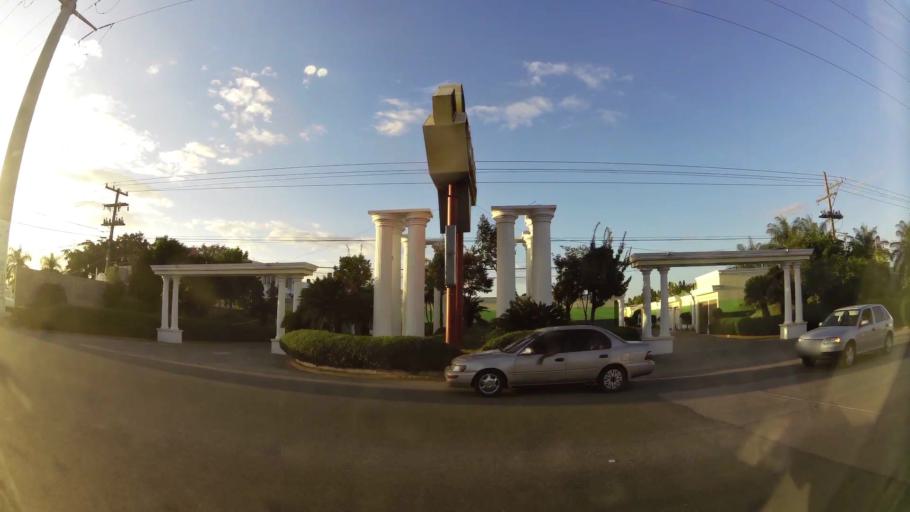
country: DO
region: Santo Domingo
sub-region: Santo Domingo
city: Santo Domingo Este
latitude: 18.4900
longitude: -69.8230
